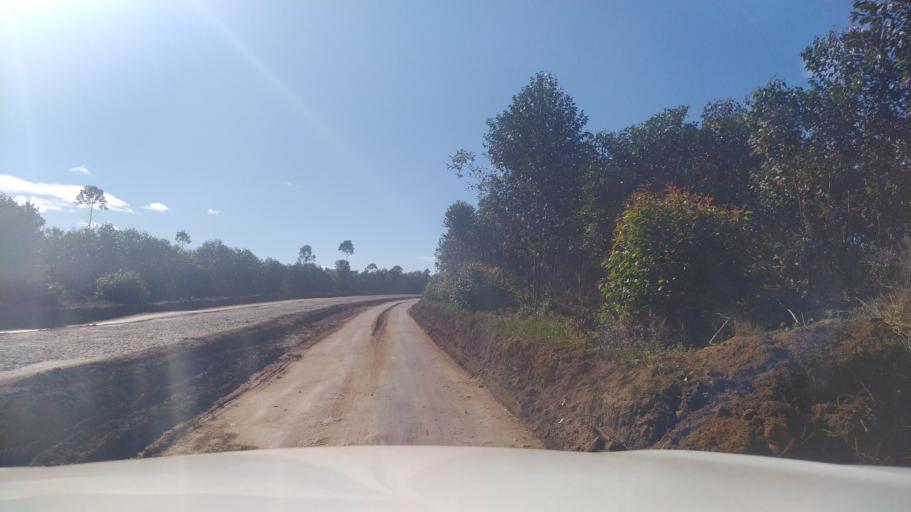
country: MG
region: Analamanga
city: Anjozorobe
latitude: -18.5355
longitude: 48.2581
